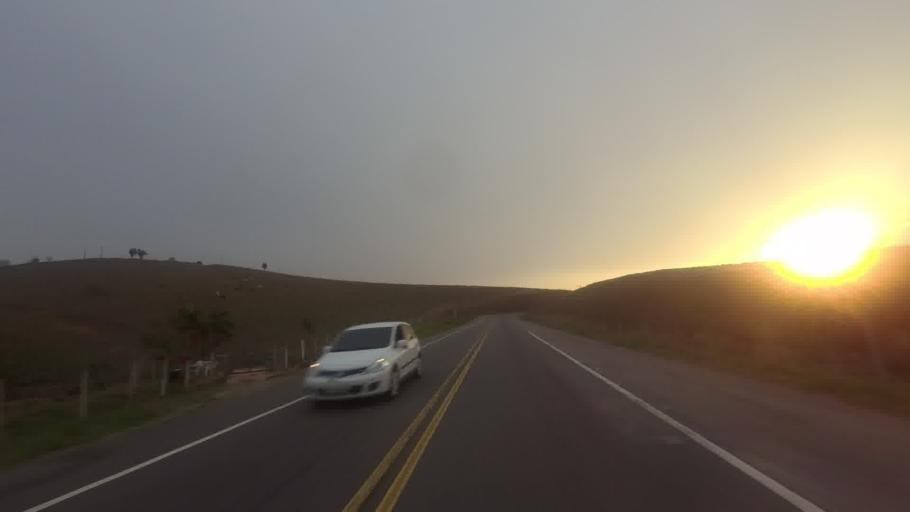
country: BR
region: Minas Gerais
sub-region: Recreio
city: Recreio
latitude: -21.7219
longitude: -42.4402
